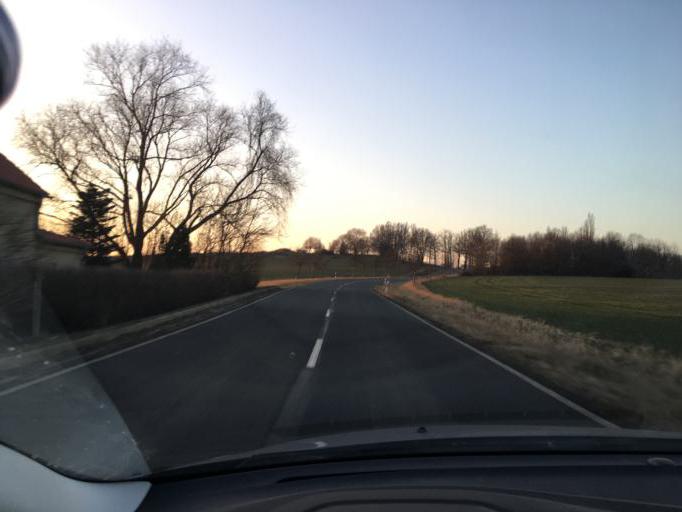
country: DE
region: Saxony
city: Lunzenau
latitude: 50.9712
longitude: 12.7453
